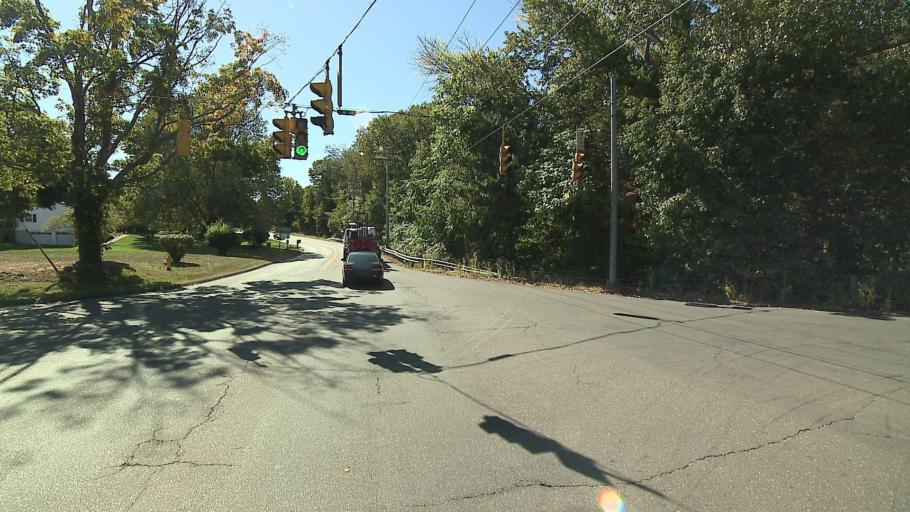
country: US
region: Connecticut
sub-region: New Haven County
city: Orange
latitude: 41.2661
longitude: -73.0504
